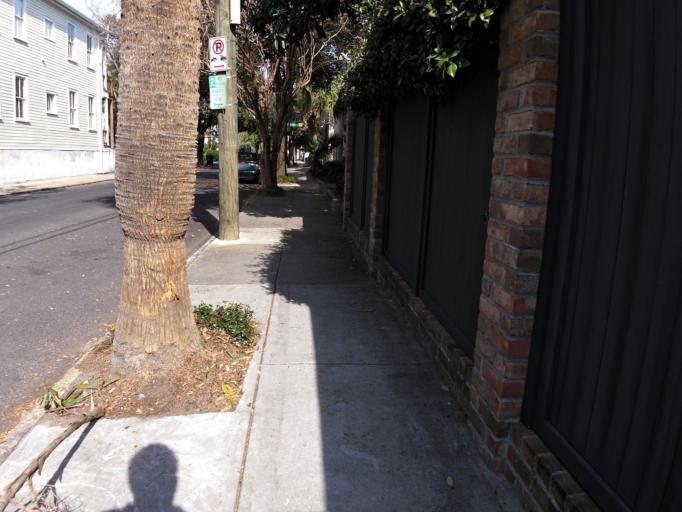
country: US
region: South Carolina
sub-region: Charleston County
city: Charleston
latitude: 32.7775
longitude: -79.9360
